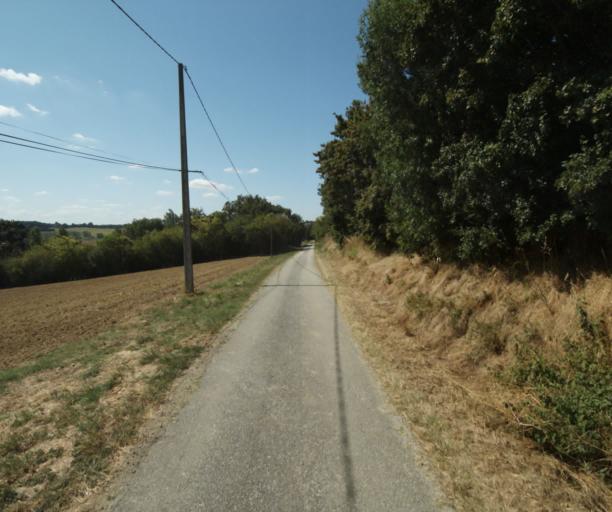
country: FR
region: Midi-Pyrenees
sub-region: Departement de la Haute-Garonne
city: Saint-Felix-Lauragais
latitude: 43.4907
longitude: 1.8865
